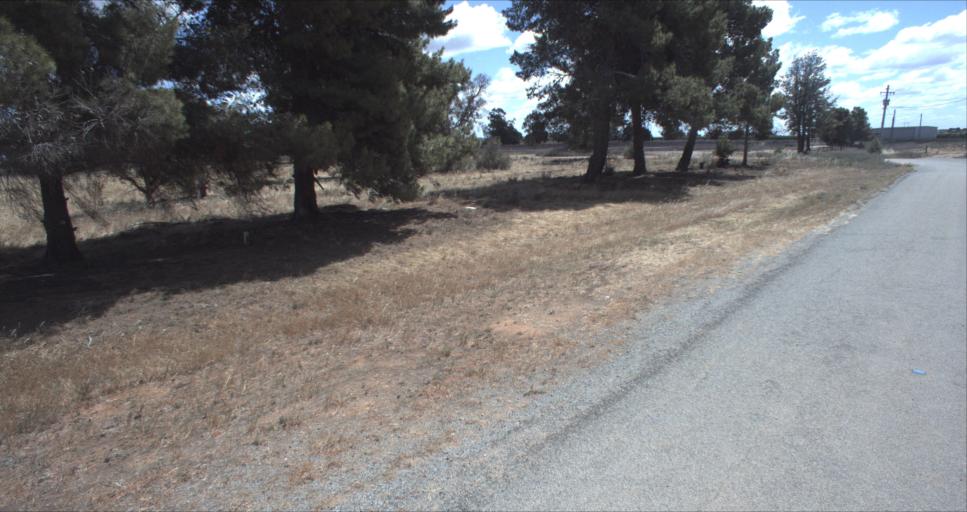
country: AU
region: New South Wales
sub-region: Murrumbidgee Shire
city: Darlington Point
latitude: -34.5110
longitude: 146.1848
